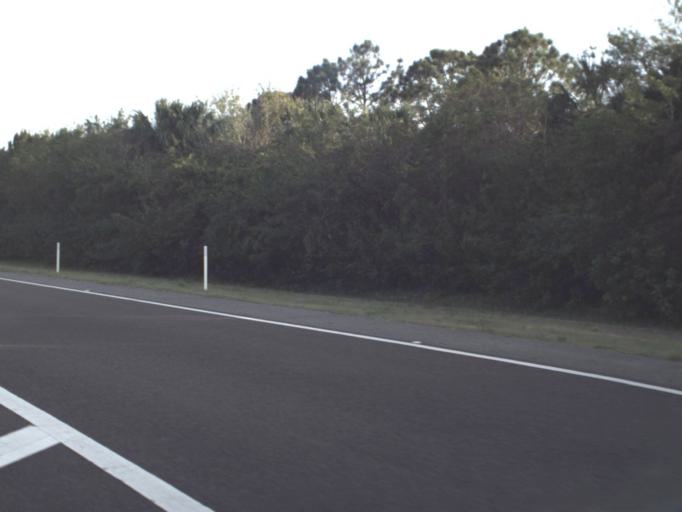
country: US
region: Florida
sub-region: Brevard County
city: Port Saint John
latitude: 28.5070
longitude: -80.8432
